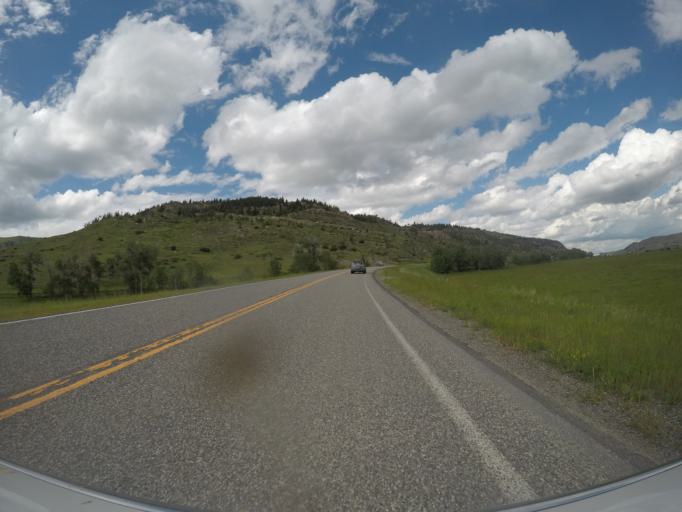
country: US
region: Montana
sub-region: Sweet Grass County
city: Big Timber
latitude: 45.6648
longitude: -110.1126
